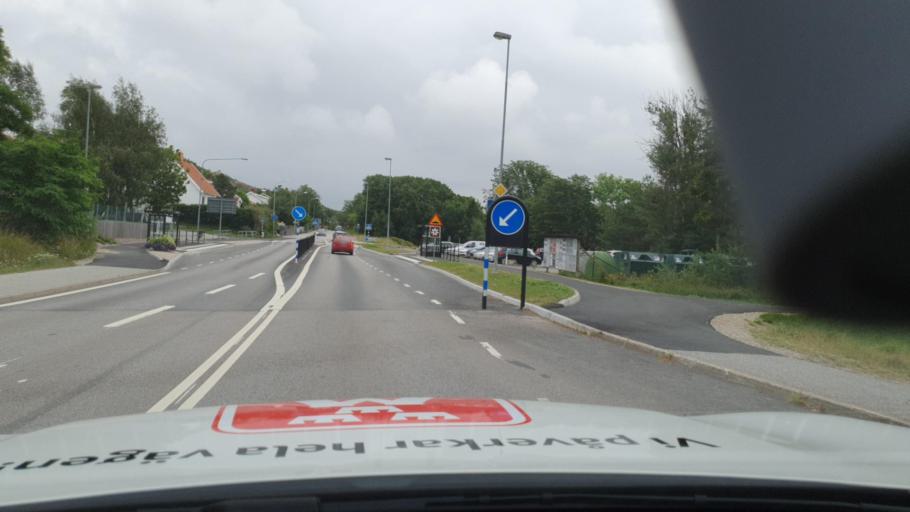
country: SE
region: Vaestra Goetaland
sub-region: Sotenas Kommun
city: Hunnebostrand
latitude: 58.4745
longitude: 11.3265
